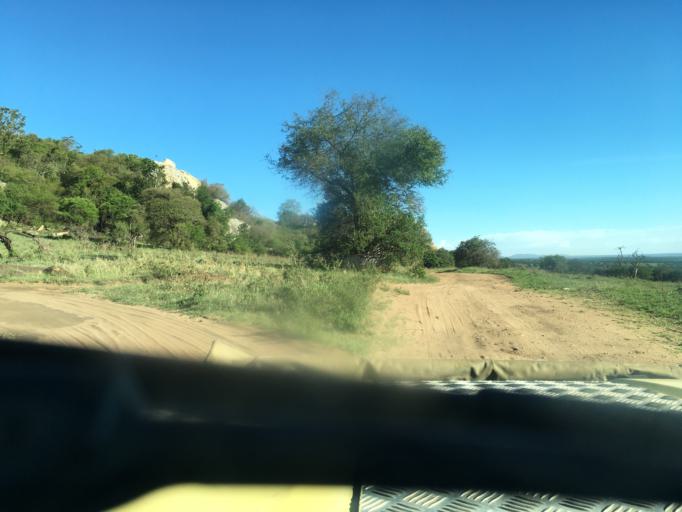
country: TZ
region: Mara
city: Mugumu
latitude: -2.0008
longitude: 35.1658
